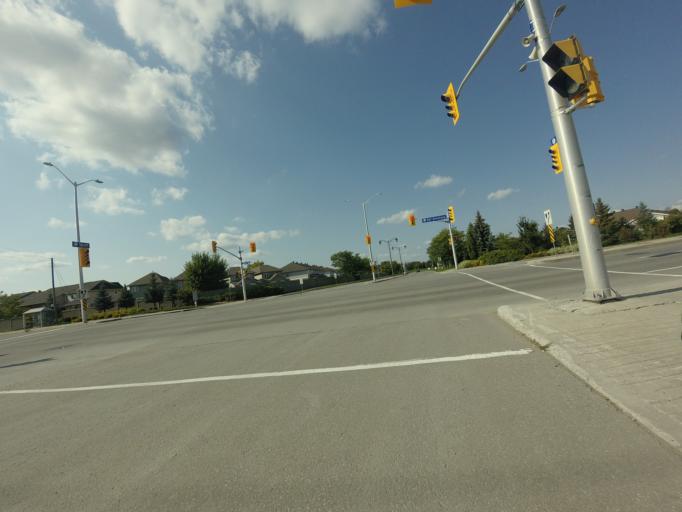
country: CA
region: Ontario
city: Ottawa
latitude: 45.2720
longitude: -75.6893
